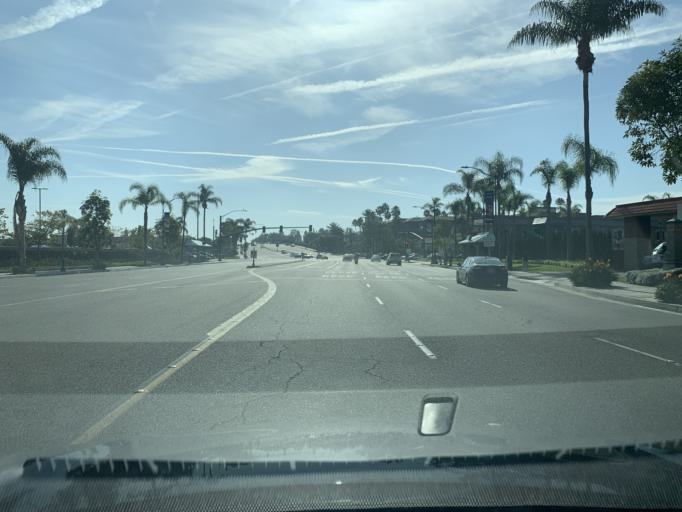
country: US
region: California
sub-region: Orange County
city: Anaheim
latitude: 33.8193
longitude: -117.9151
